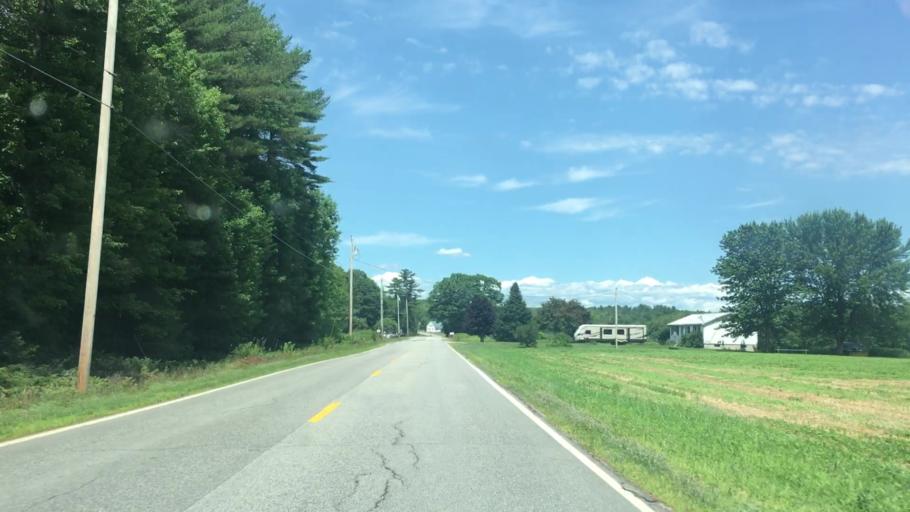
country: US
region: Maine
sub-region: Androscoggin County
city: Livermore
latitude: 44.3467
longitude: -70.1926
